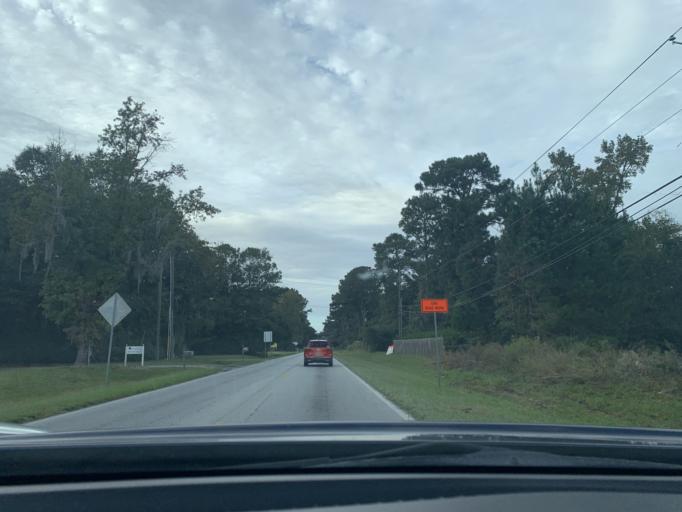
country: US
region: Georgia
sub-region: Chatham County
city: Georgetown
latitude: 32.0192
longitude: -81.2386
